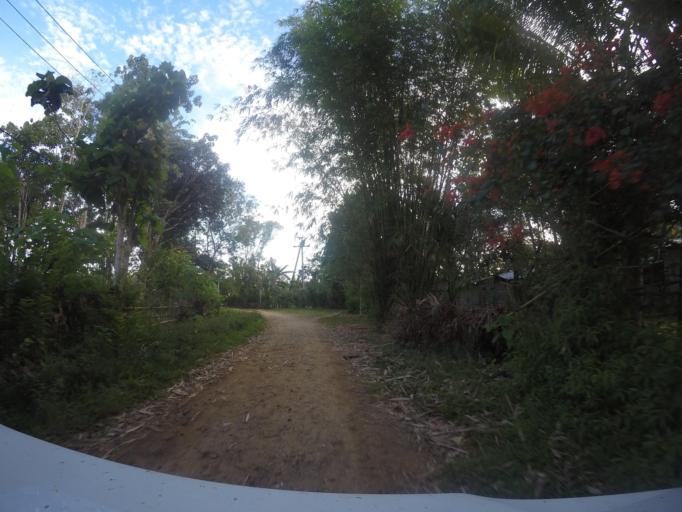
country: TL
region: Lautem
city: Lospalos
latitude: -8.5134
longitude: 126.9926
